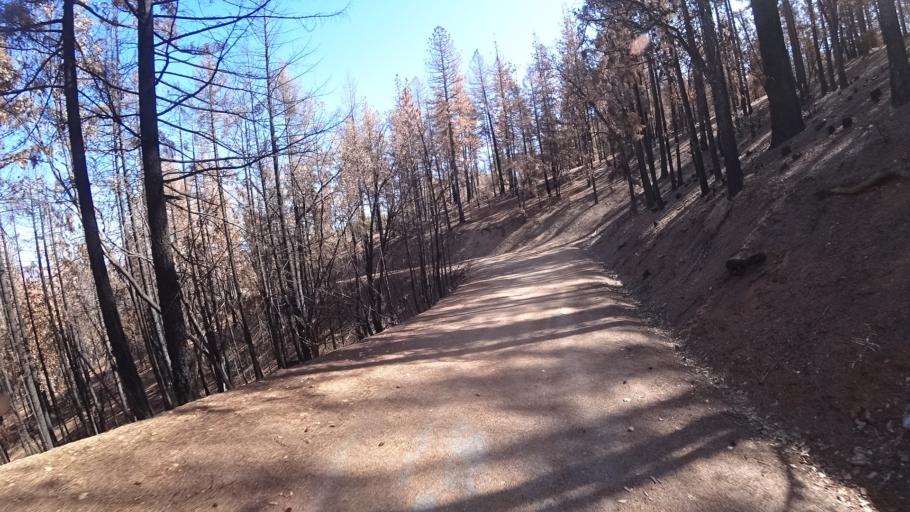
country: US
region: California
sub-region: Tehama County
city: Rancho Tehama Reserve
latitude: 39.6640
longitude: -122.7125
